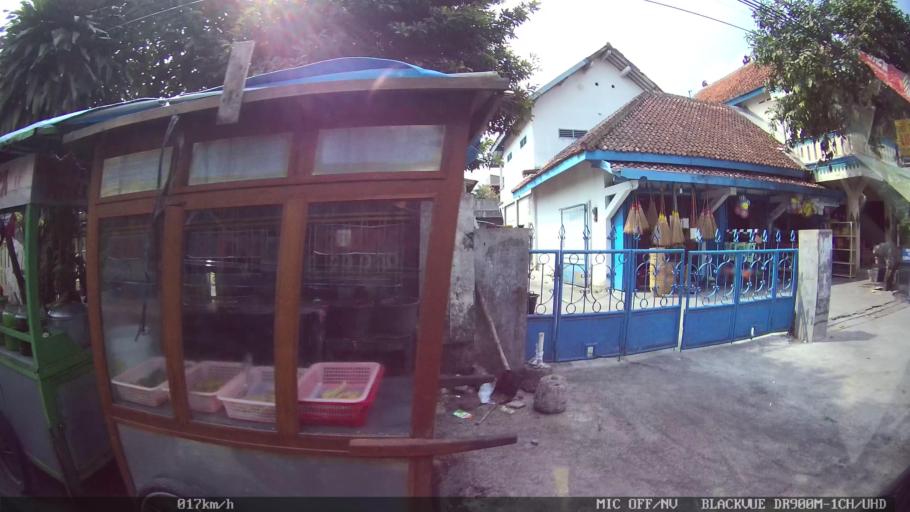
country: ID
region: Daerah Istimewa Yogyakarta
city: Depok
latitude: -7.8027
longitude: 110.4129
